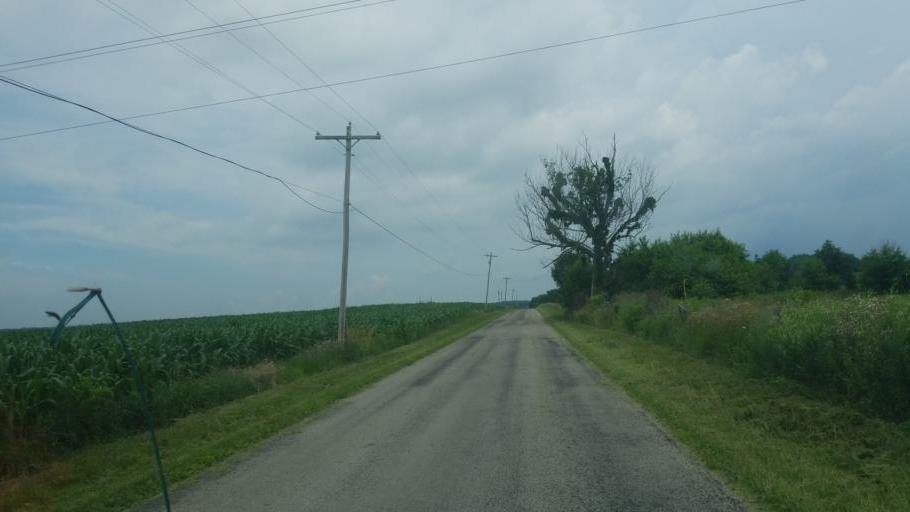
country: US
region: Ohio
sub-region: Wayne County
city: Wooster
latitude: 40.8667
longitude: -81.9934
